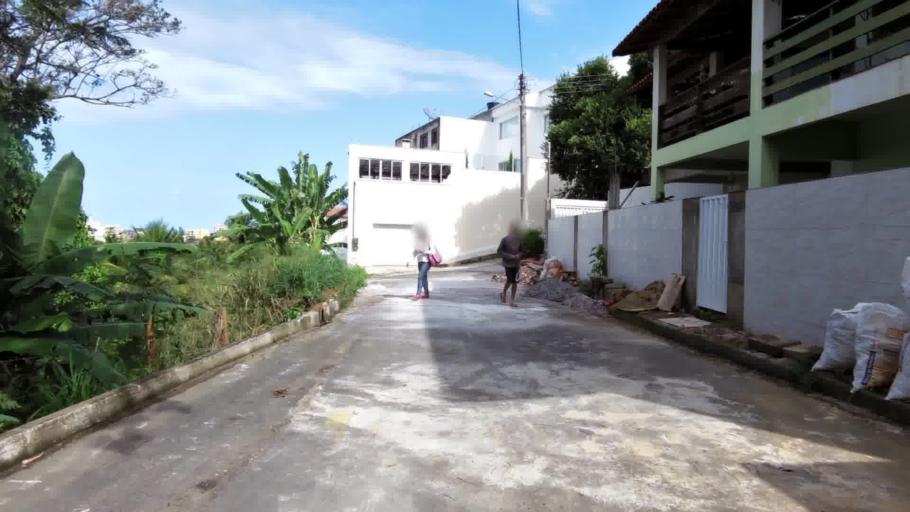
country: BR
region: Espirito Santo
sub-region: Piuma
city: Piuma
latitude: -20.8286
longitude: -40.6971
